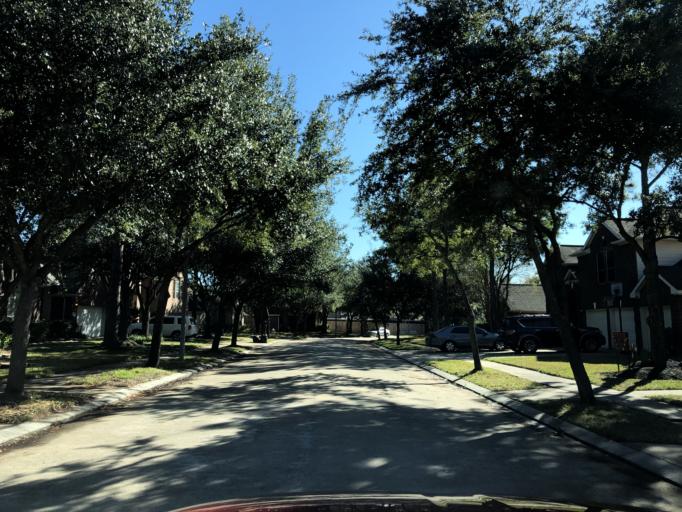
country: US
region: Texas
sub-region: Harris County
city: Oak Cliff Place
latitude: 29.9433
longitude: -95.6629
